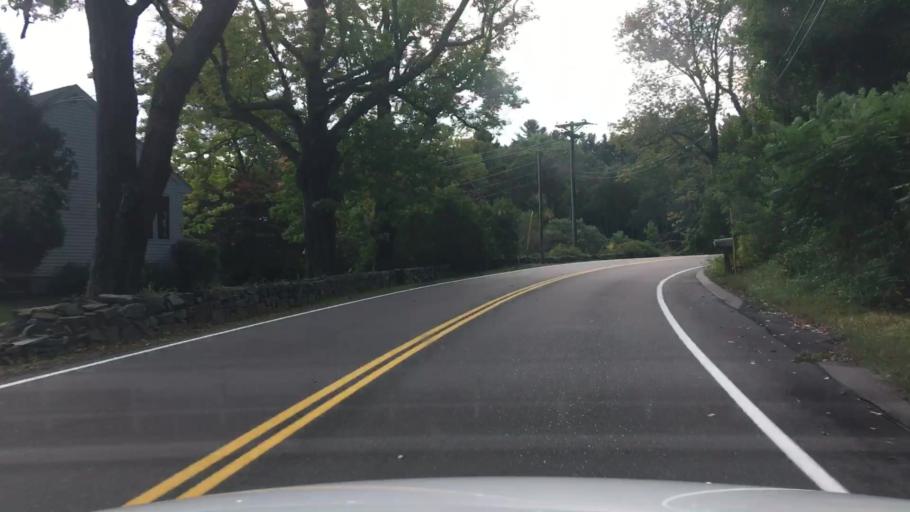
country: US
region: Maine
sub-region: York County
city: Kittery Point
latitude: 43.0928
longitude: -70.7015
